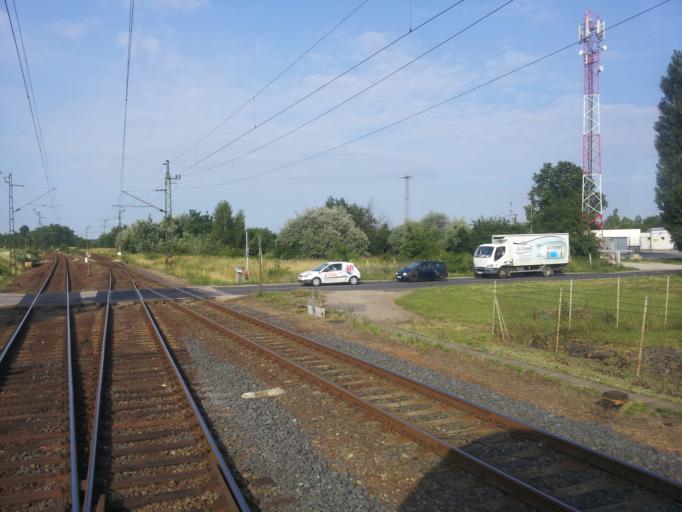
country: HU
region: Fejer
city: Szabadbattyan
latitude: 47.1032
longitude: 18.3847
